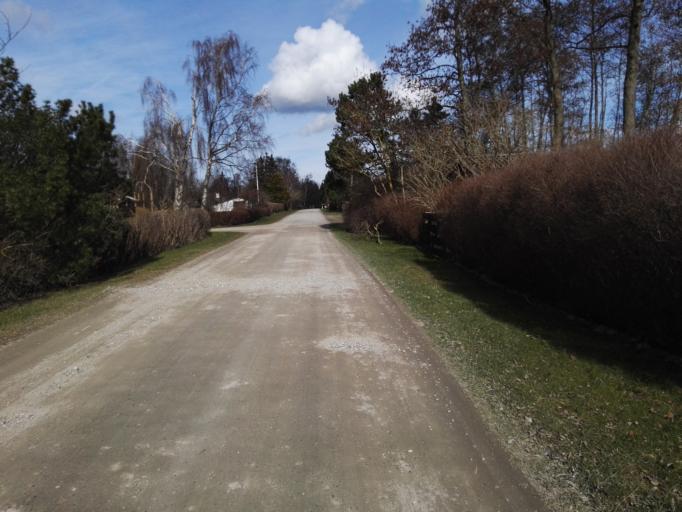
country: DK
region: Zealand
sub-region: Lejre Kommune
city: Ejby
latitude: 55.7606
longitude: 11.8315
